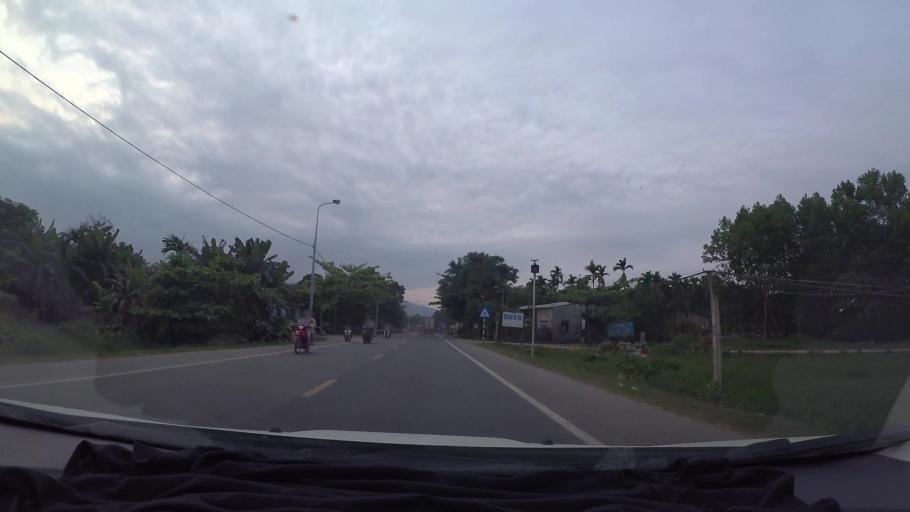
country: VN
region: Da Nang
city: Lien Chieu
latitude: 16.0542
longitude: 108.1026
